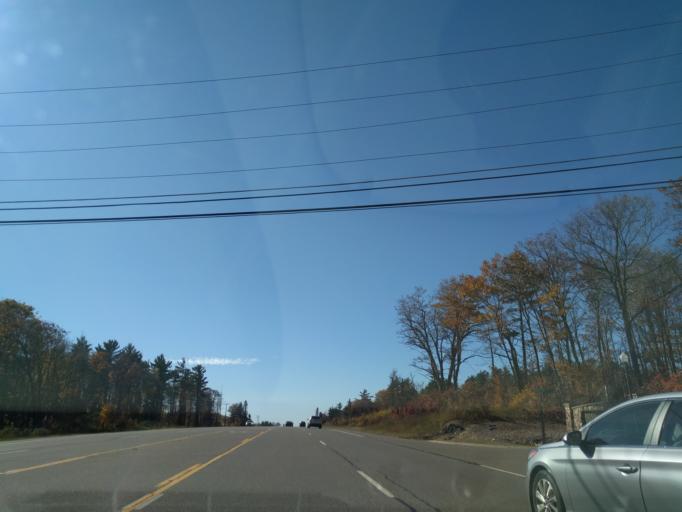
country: US
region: Michigan
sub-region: Marquette County
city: Ishpeming
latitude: 46.5101
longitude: -87.6457
